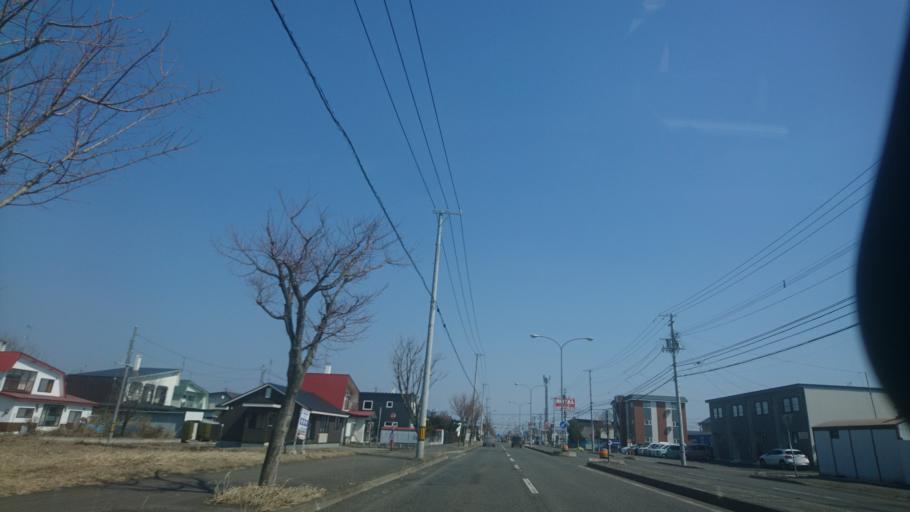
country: JP
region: Hokkaido
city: Obihiro
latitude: 42.9157
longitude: 143.1146
